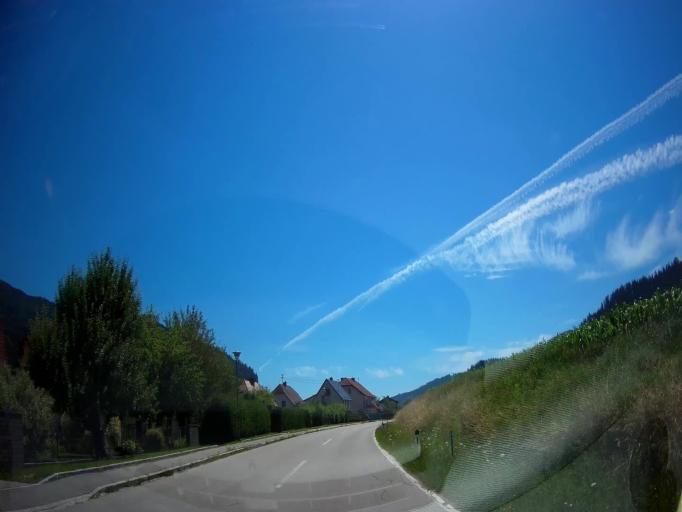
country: AT
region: Carinthia
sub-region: Politischer Bezirk Sankt Veit an der Glan
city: Micheldorf
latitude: 46.9118
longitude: 14.4332
